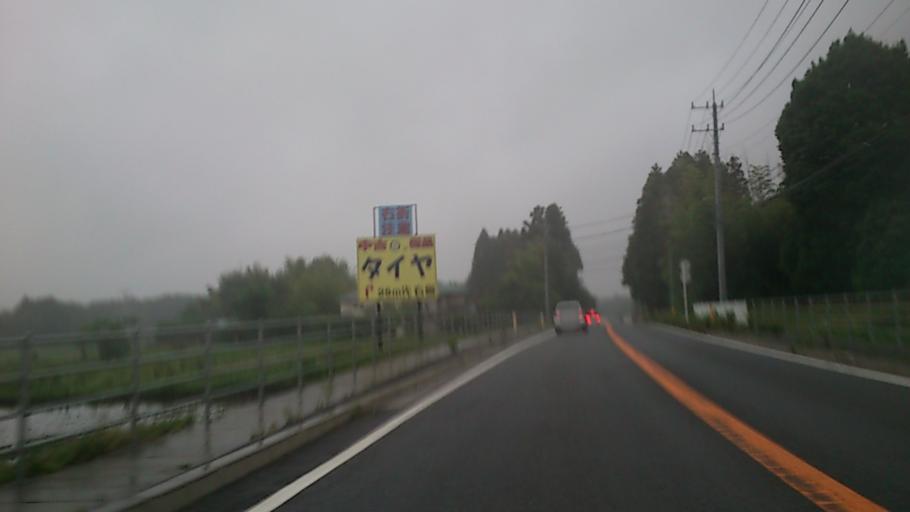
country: JP
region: Tochigi
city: Kuroiso
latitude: 37.0496
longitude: 140.1042
